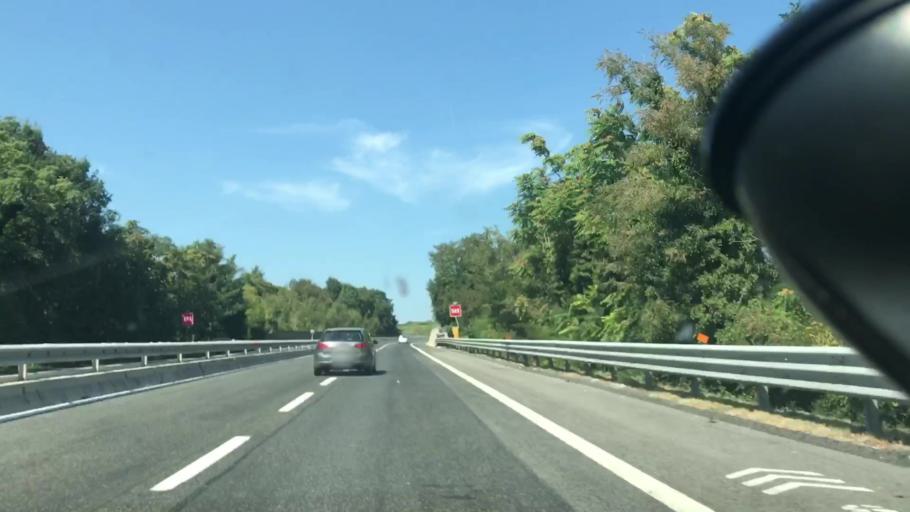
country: IT
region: Abruzzo
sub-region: Provincia di Chieti
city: Casalbordino-Miracoli
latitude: 42.1632
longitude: 14.6323
